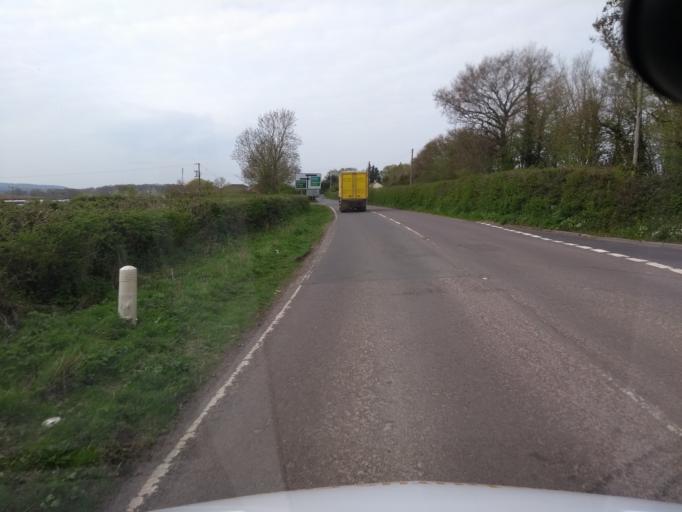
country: GB
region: England
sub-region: Somerset
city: Creech Saint Michael
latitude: 51.0008
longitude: -3.0161
